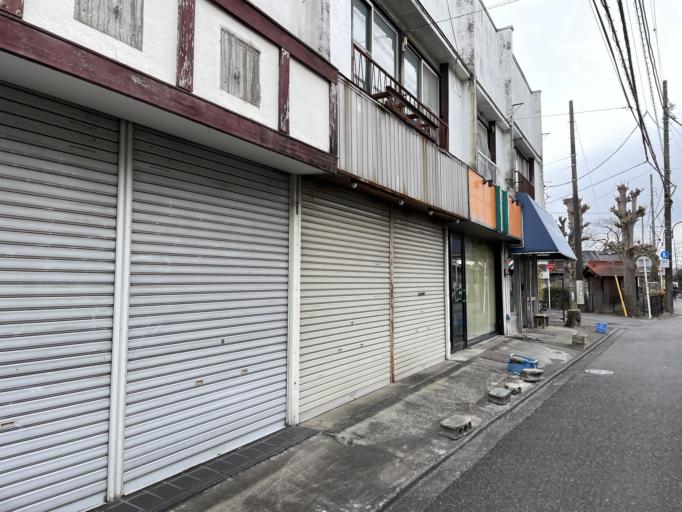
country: JP
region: Tokyo
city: Chofugaoka
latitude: 35.6328
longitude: 139.5919
